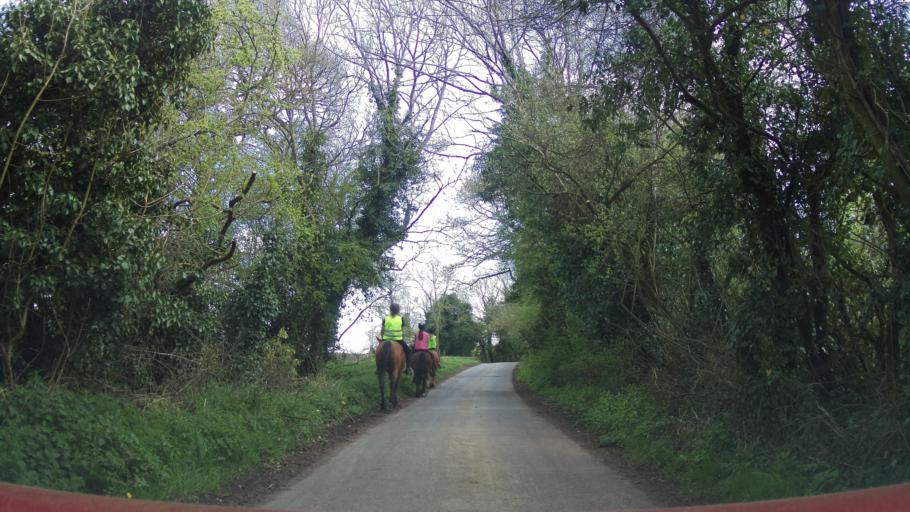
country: GB
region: England
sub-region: South Gloucestershire
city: Tytherington
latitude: 51.5704
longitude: -2.4885
